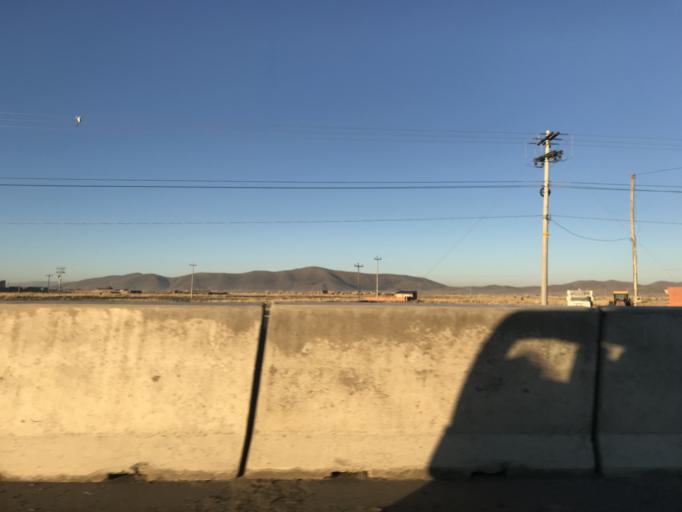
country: BO
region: La Paz
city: Batallas
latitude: -16.2953
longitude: -68.5371
